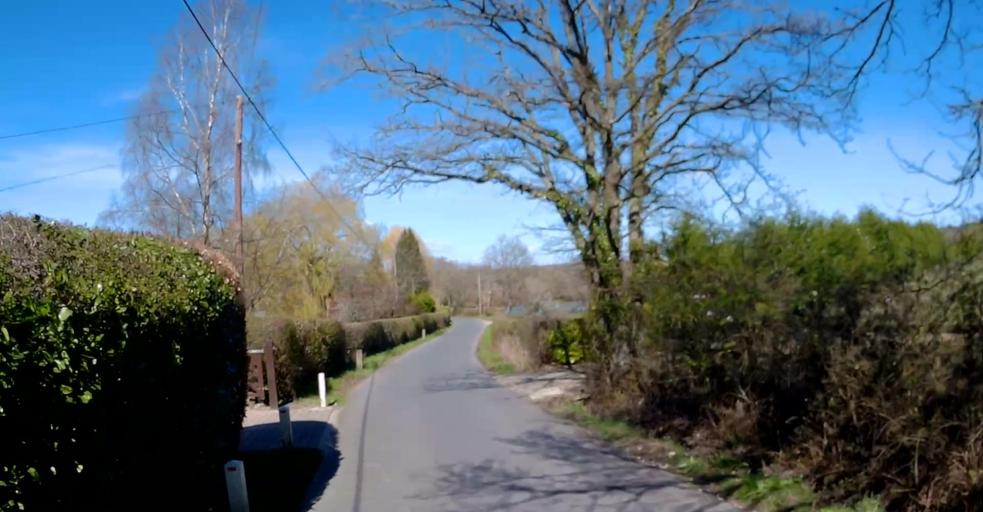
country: GB
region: England
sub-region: Hampshire
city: Lindford
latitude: 51.1649
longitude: -0.8289
